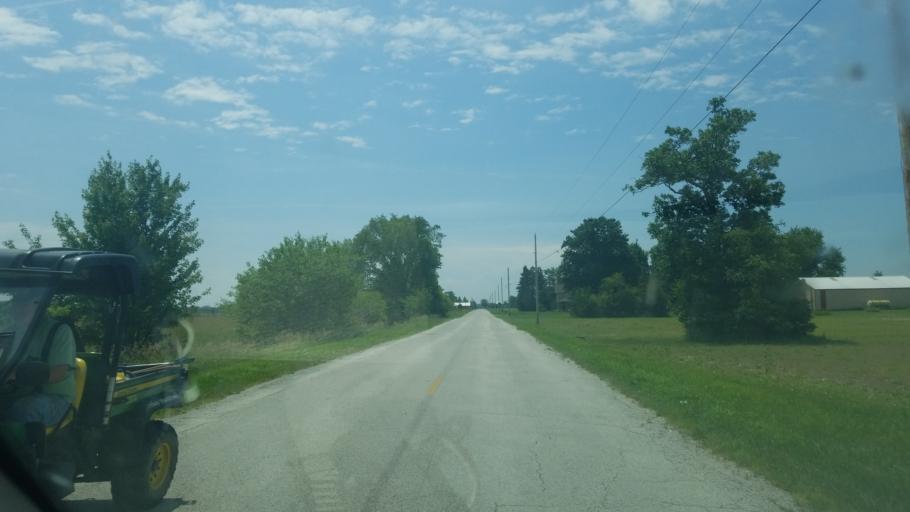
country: US
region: Ohio
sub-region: Wood County
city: North Baltimore
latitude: 41.2169
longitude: -83.5924
